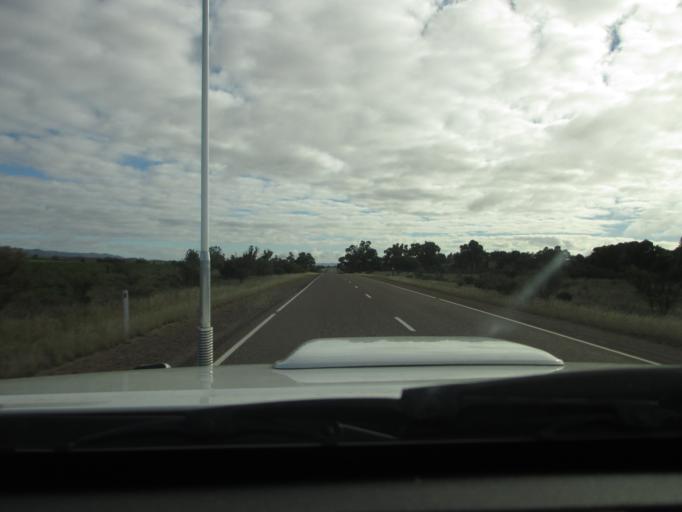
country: AU
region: South Australia
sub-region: Flinders Ranges
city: Quorn
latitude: -32.4806
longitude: 138.5429
